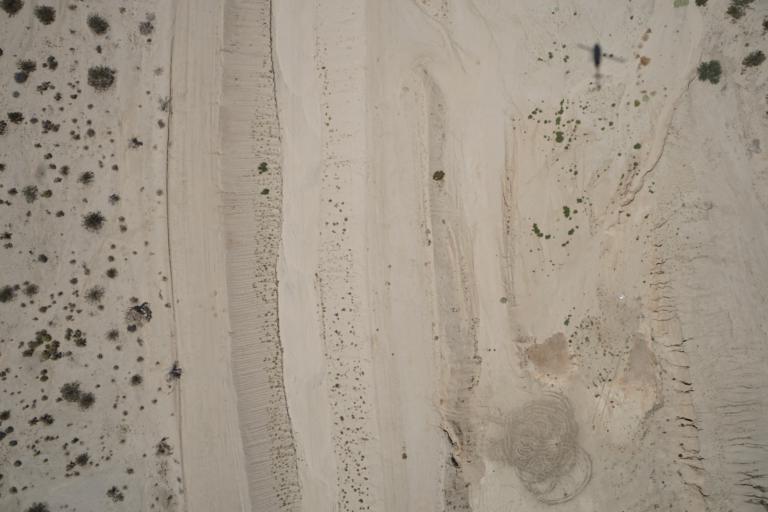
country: US
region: California
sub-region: San Bernardino County
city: Twentynine Palms
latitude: 34.1385
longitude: -116.0658
